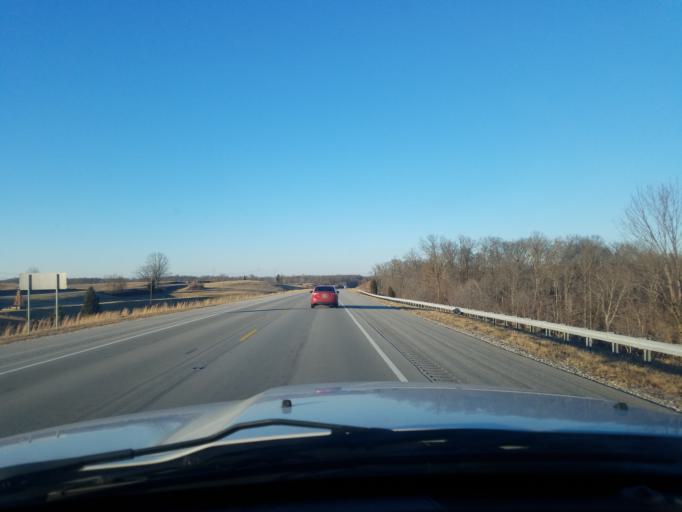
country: US
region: Indiana
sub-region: Crawford County
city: English
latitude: 38.1686
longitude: -86.6047
